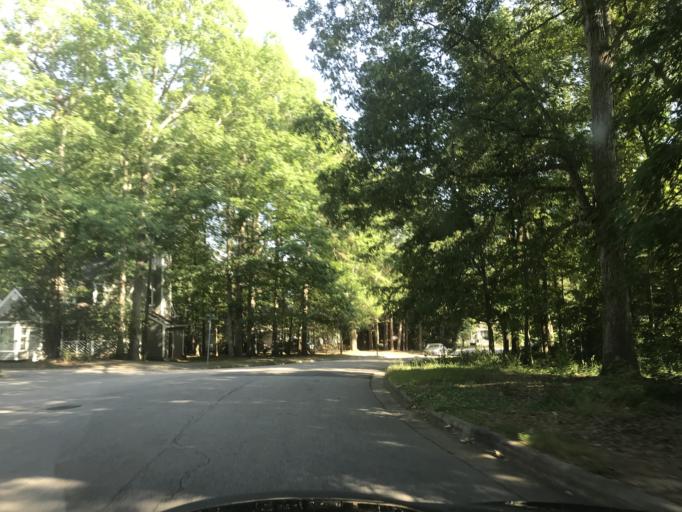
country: US
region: North Carolina
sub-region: Wake County
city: West Raleigh
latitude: 35.8641
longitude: -78.6170
